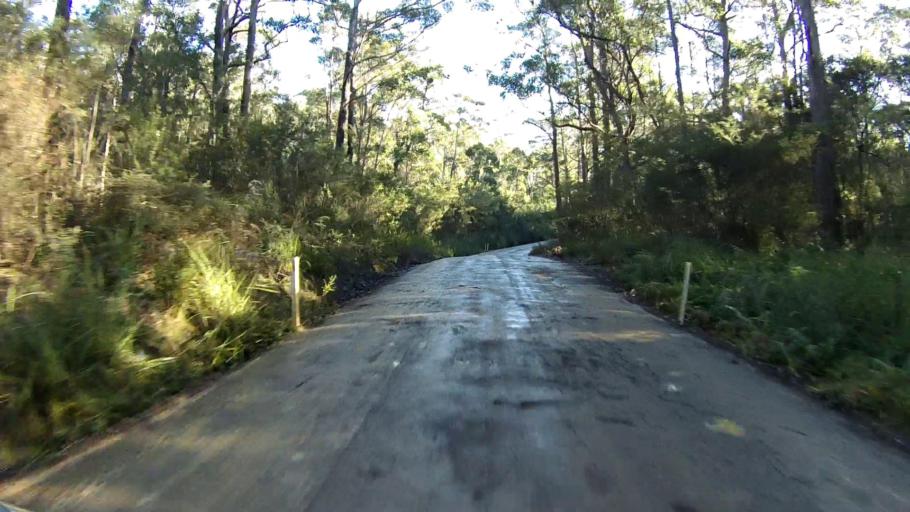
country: AU
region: Tasmania
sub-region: Clarence
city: Sandford
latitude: -43.1449
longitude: 147.9586
